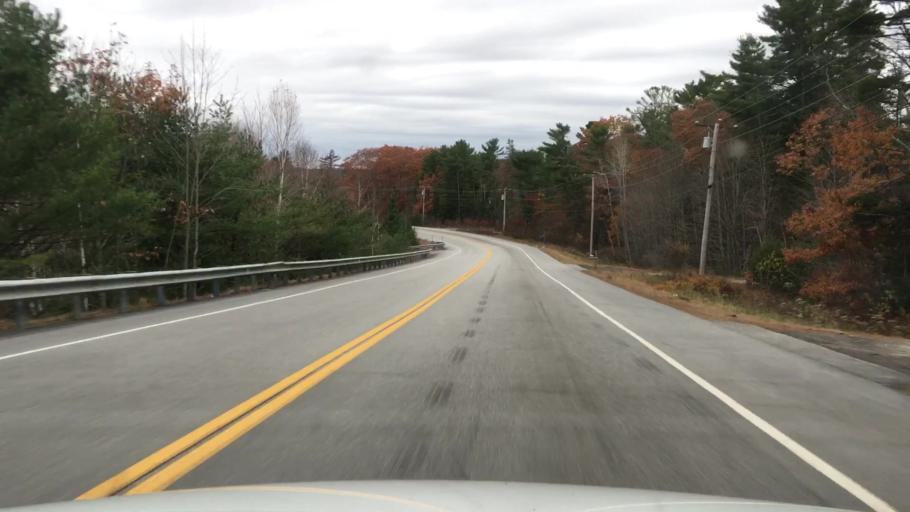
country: US
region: Maine
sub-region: Hancock County
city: Orland
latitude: 44.5565
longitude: -68.6973
